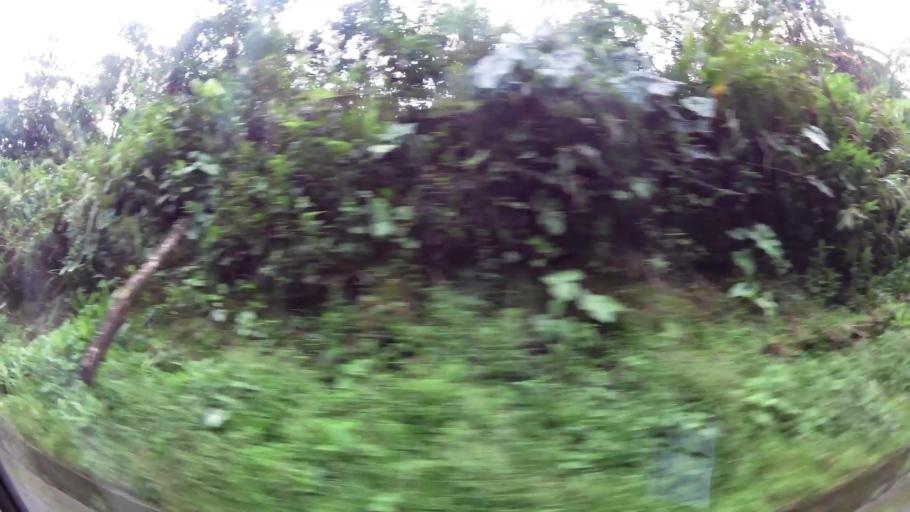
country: EC
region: Pastaza
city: Puyo
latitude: -1.4271
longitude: -78.1767
